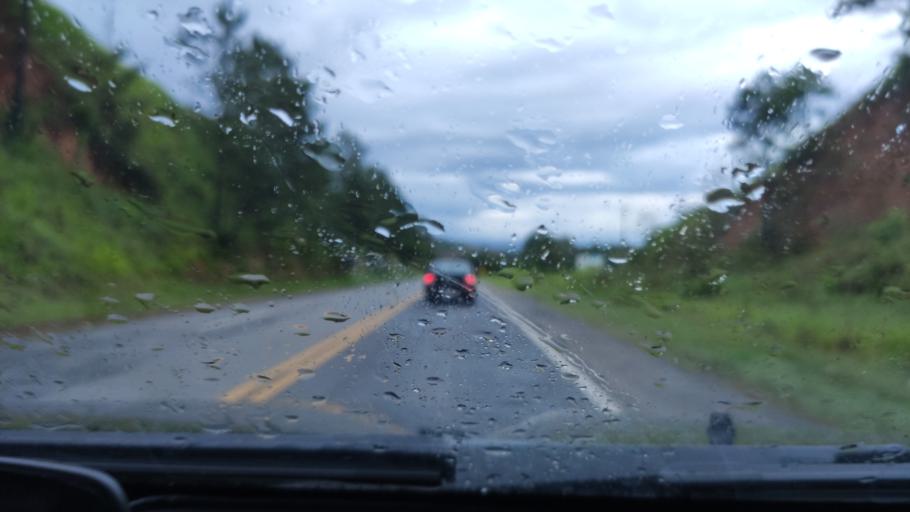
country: BR
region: Sao Paulo
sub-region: Braganca Paulista
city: Braganca Paulista
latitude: -22.8109
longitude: -46.5488
